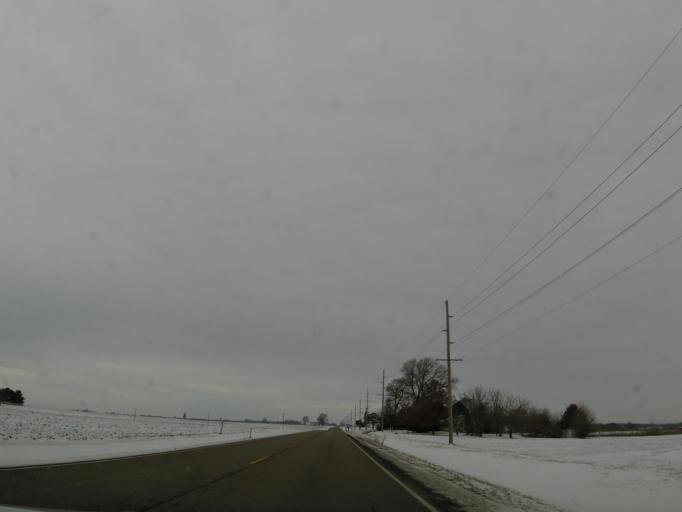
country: US
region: Illinois
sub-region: LaSalle County
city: Oglesby
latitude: 41.2650
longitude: -89.0928
